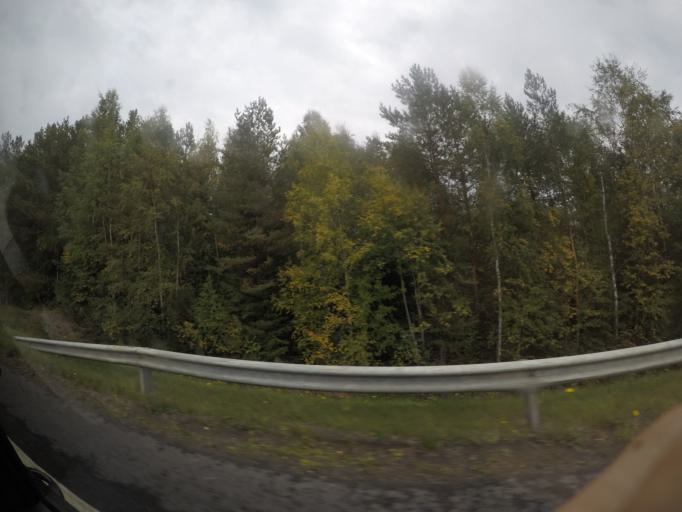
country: FI
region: Haeme
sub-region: Haemeenlinna
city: Parola
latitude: 61.1250
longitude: 24.4182
